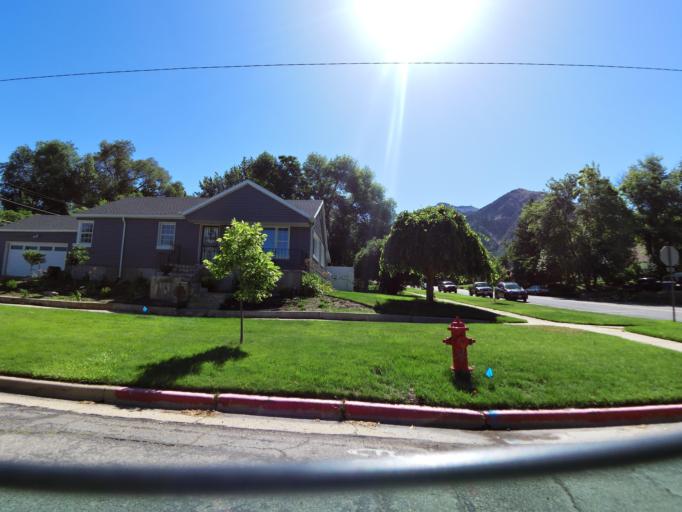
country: US
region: Utah
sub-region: Weber County
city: Ogden
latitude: 41.2162
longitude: -111.9428
